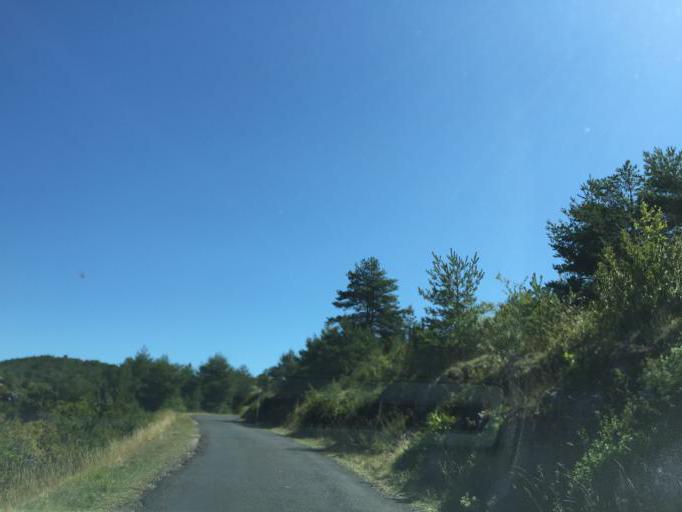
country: FR
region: Midi-Pyrenees
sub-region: Departement de l'Aveyron
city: La Cavalerie
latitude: 43.9050
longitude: 3.2866
